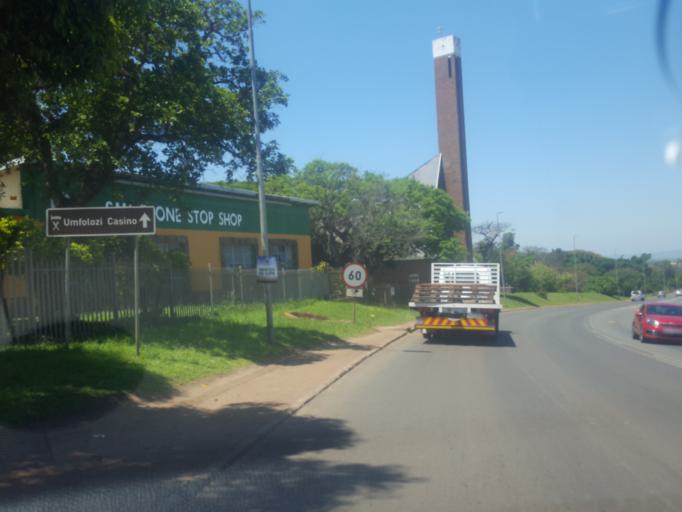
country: ZA
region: KwaZulu-Natal
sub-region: uThungulu District Municipality
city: Empangeni
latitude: -28.7459
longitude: 31.8911
